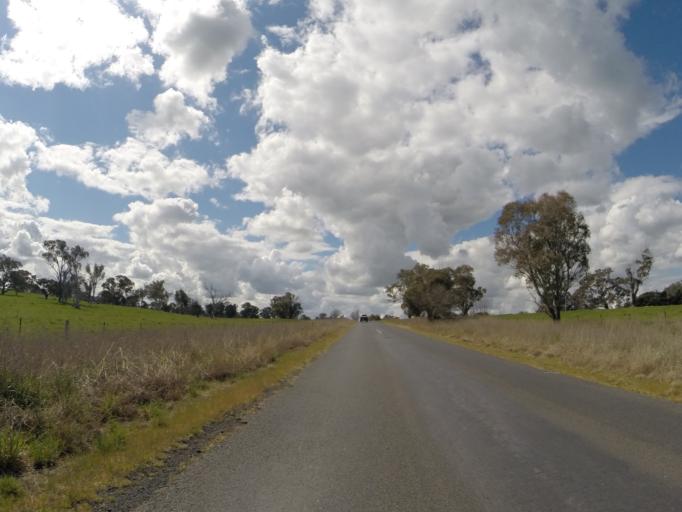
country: AU
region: New South Wales
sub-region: Yass Valley
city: Yass
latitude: -34.9363
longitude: 148.8740
